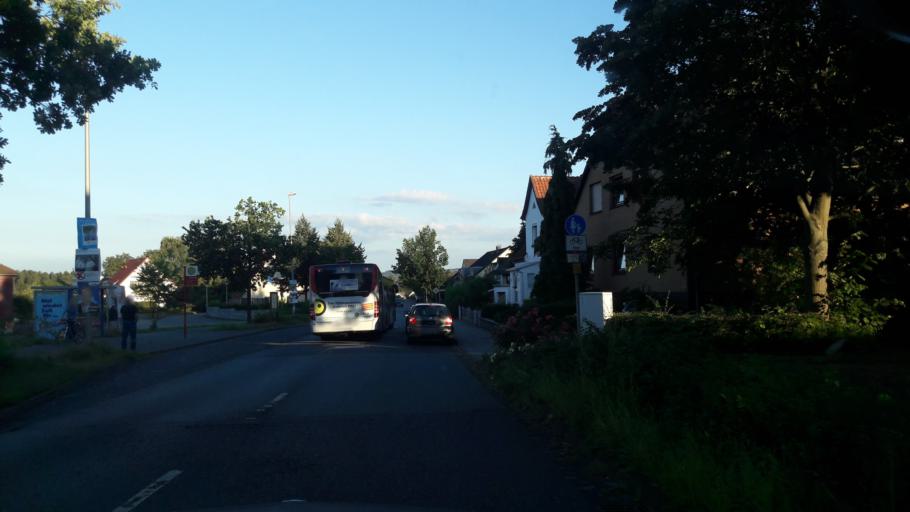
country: DE
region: Lower Saxony
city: Hildesheim
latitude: 52.1191
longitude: 9.9911
